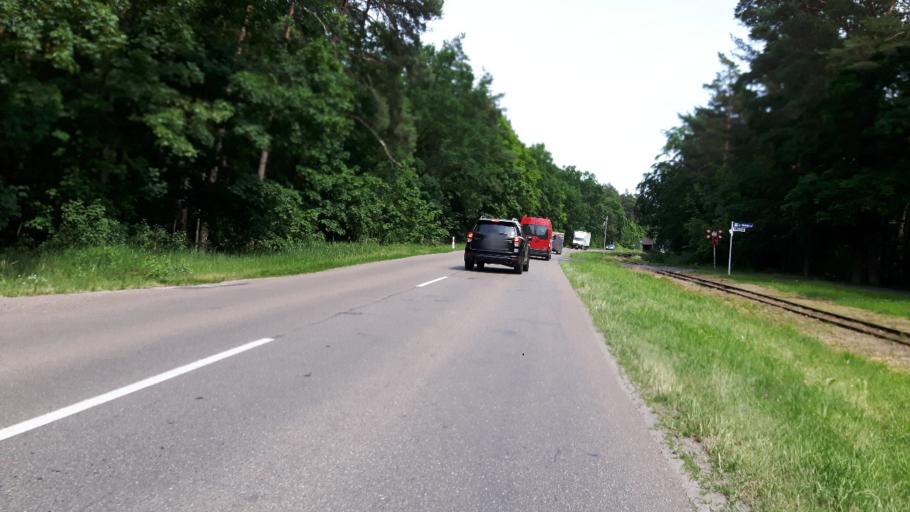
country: PL
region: Pomeranian Voivodeship
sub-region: Powiat nowodworski
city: Stegna
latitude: 54.3322
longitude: 19.0717
